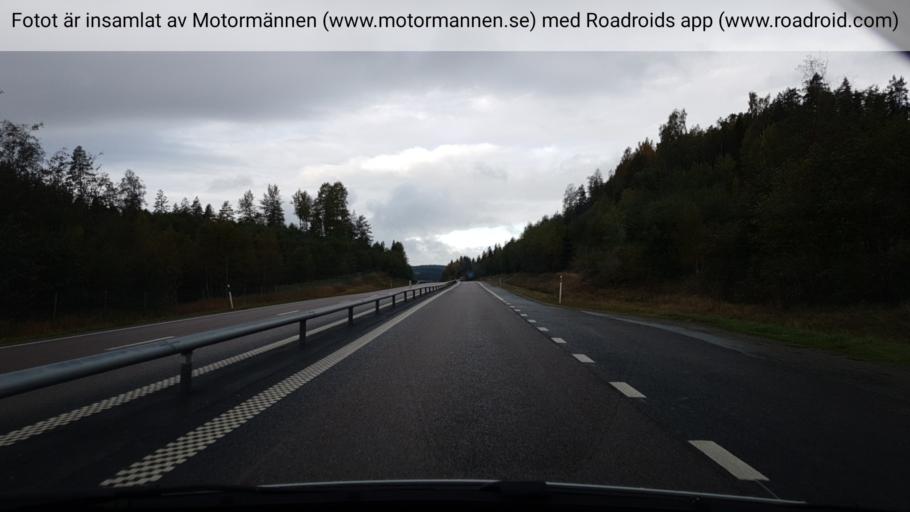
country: SE
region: Vaesternorrland
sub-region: OErnskoeldsviks Kommun
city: Ornskoldsvik
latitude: 63.3134
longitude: 18.8184
